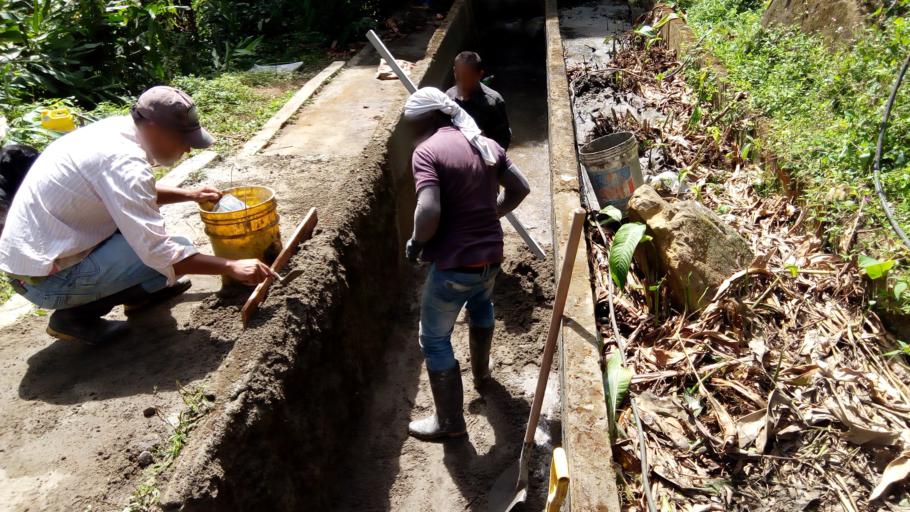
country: CO
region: Valle del Cauca
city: Jamundi
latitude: 3.3246
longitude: -76.6264
